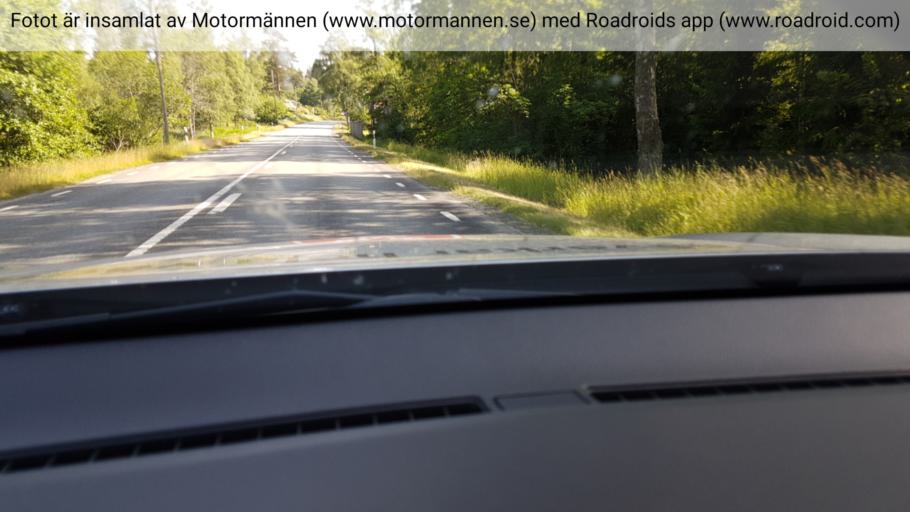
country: SE
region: Joenkoeping
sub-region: Eksjo Kommun
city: Eksjoe
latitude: 57.7551
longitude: 14.9252
